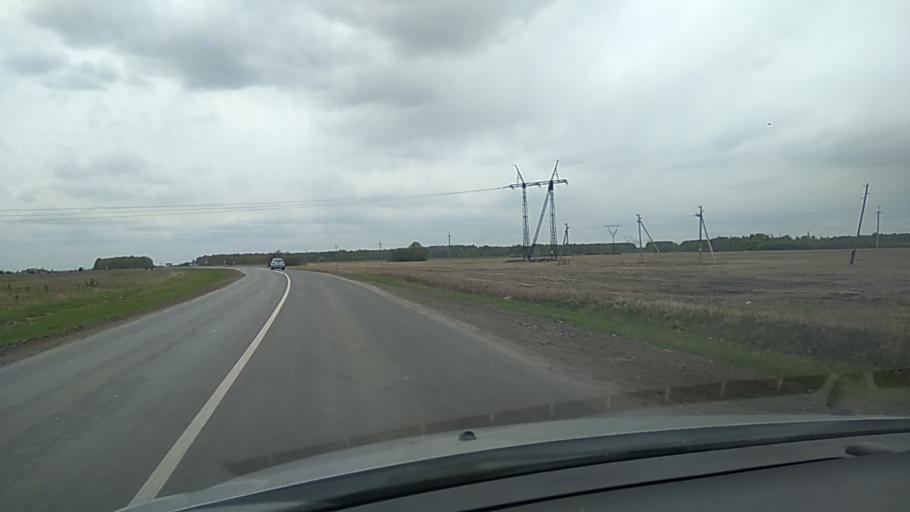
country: RU
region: Sverdlovsk
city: Martyush
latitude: 56.4110
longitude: 61.7963
